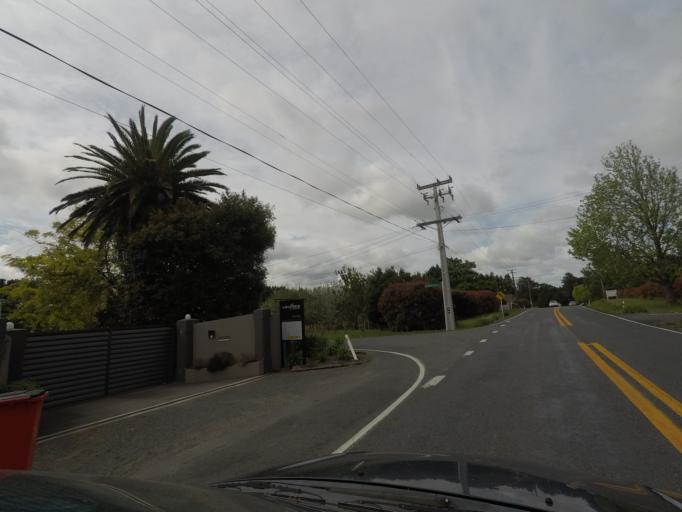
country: NZ
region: Auckland
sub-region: Auckland
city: Rosebank
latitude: -36.7682
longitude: 174.5873
